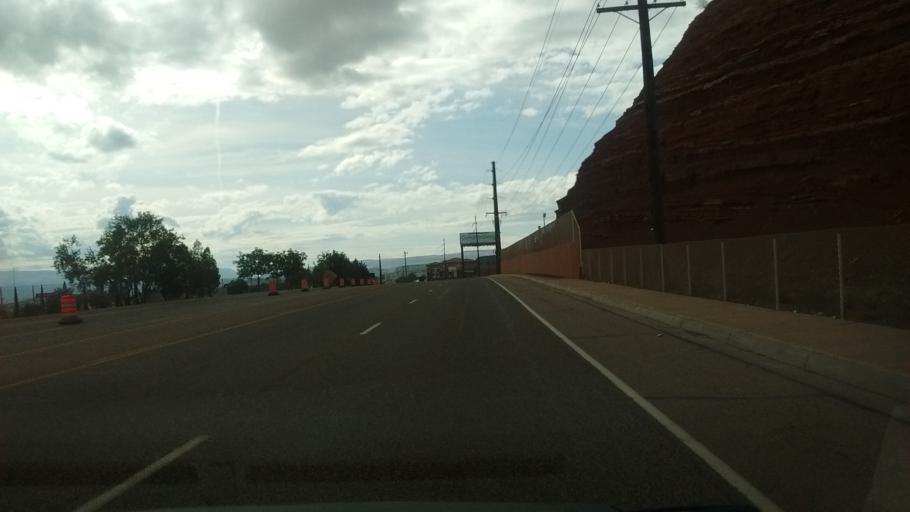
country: US
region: Utah
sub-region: Washington County
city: Saint George
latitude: 37.1169
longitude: -113.5513
